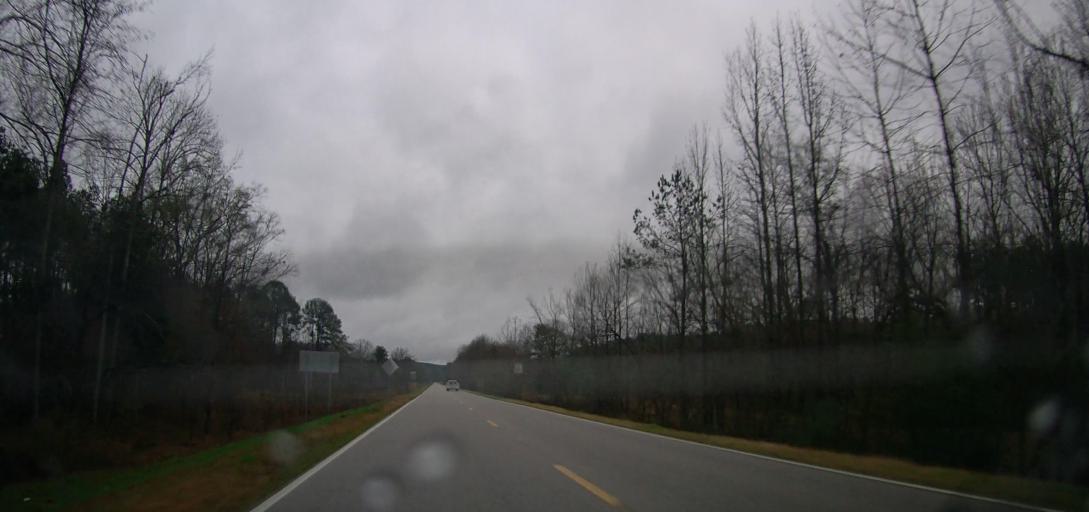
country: US
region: Alabama
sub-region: Bibb County
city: Centreville
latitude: 32.9261
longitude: -87.0450
